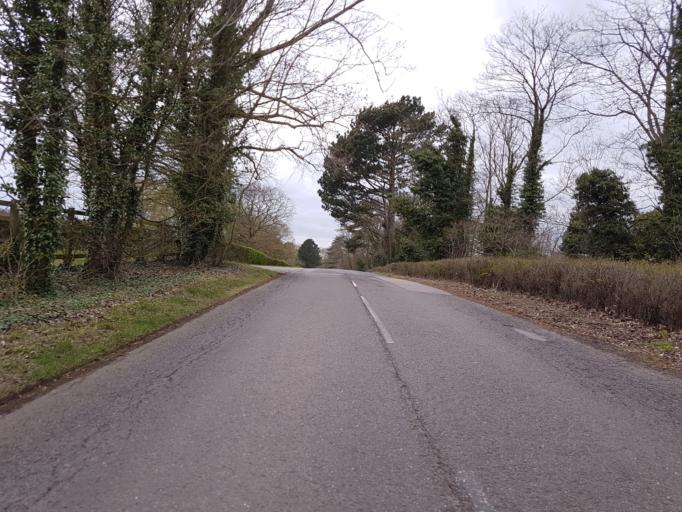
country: GB
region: England
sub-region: Cambridgeshire
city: Girton
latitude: 52.2176
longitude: 0.0590
